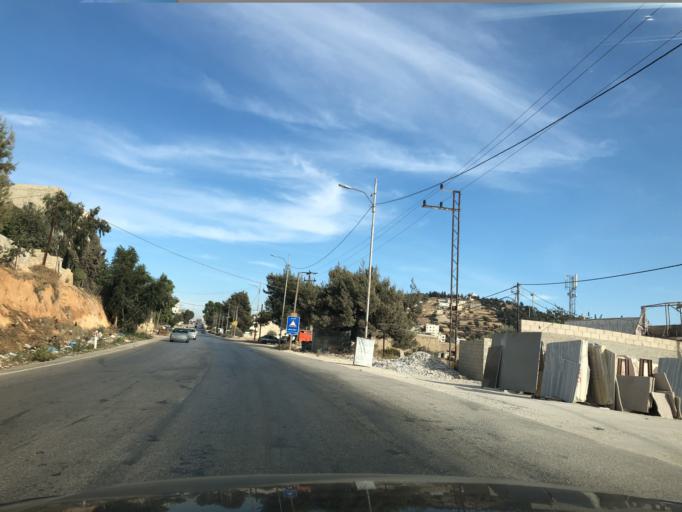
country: JO
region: Irbid
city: Sakib
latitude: 32.2796
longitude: 35.7969
